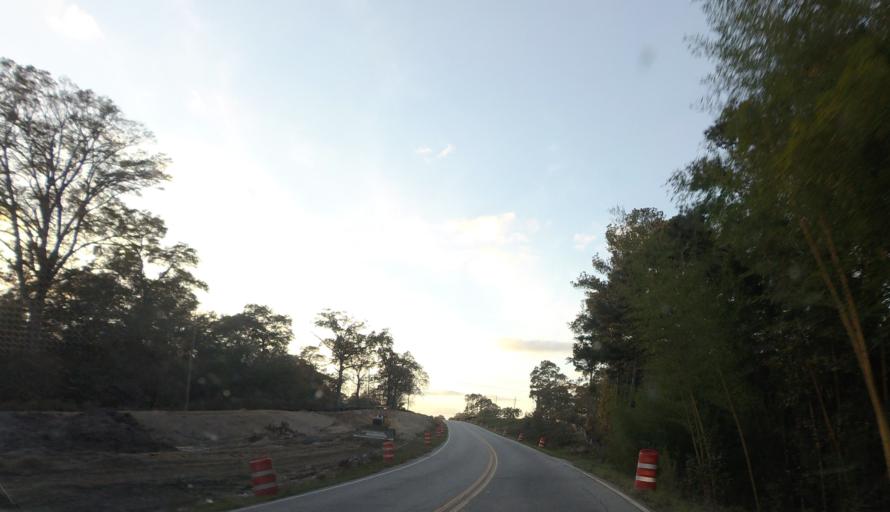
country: US
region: Georgia
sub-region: Houston County
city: Robins Air Force Base
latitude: 32.5508
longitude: -83.5803
